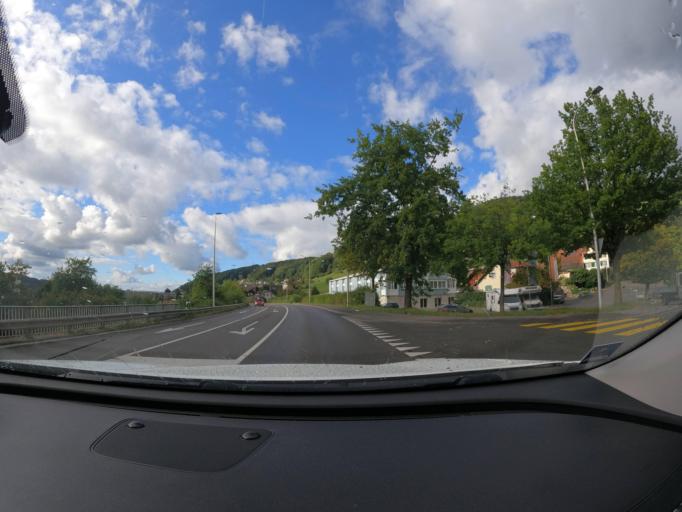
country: CH
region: Aargau
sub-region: Bezirk Kulm
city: Reinach
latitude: 47.2670
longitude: 8.1765
